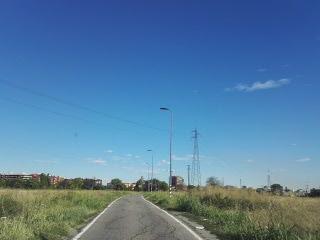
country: IT
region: Lombardy
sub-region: Citta metropolitana di Milano
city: Chiaravalle
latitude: 45.4302
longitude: 9.2123
